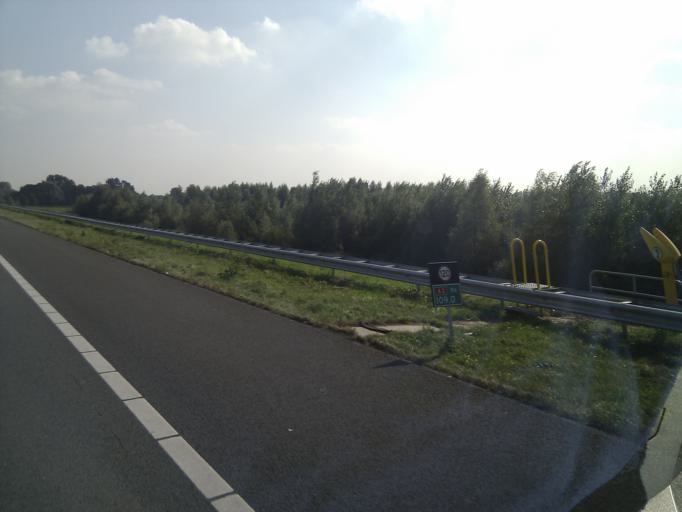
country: NL
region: Gelderland
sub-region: Gemeente Maasdriel
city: Hedel
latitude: 51.7454
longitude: 5.2969
